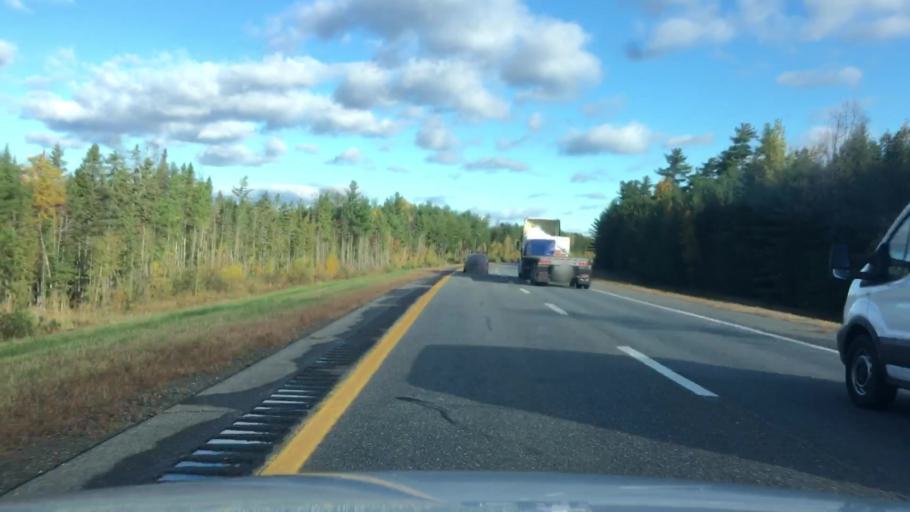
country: US
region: Maine
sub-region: Penobscot County
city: Greenbush
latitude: 45.1485
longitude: -68.7032
